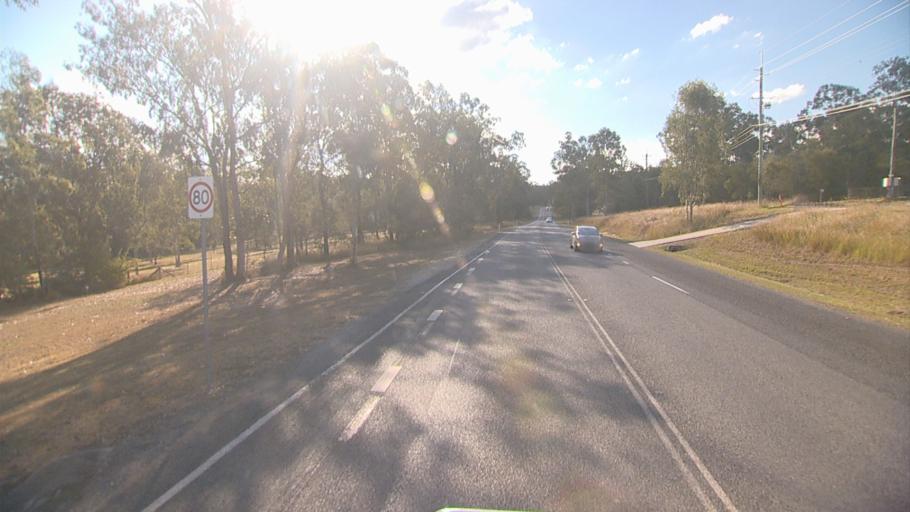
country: AU
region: Queensland
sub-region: Logan
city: North Maclean
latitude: -27.7533
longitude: 152.9871
